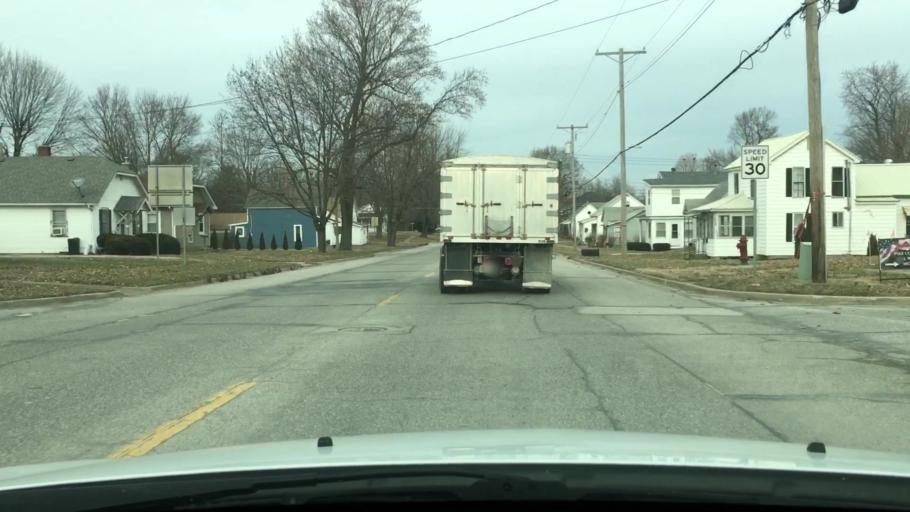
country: US
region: Illinois
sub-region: Pike County
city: Pittsfield
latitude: 39.6090
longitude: -90.8030
